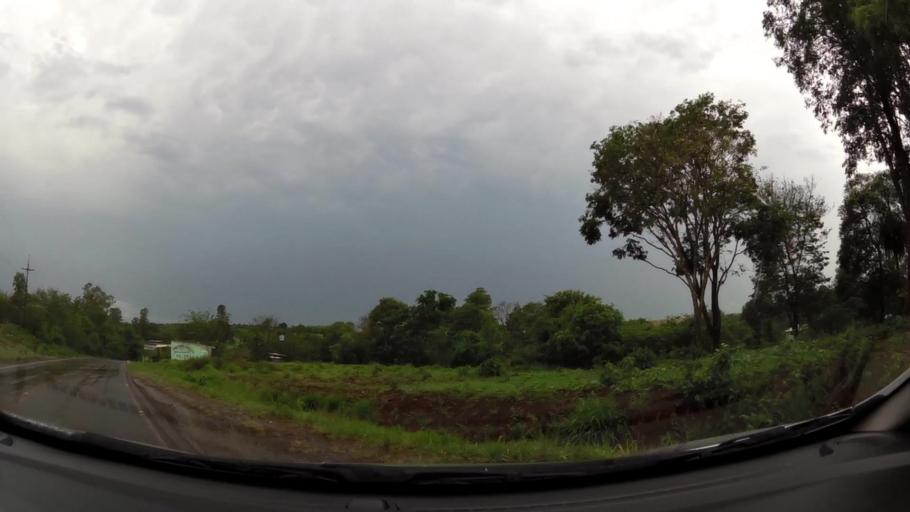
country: PY
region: Alto Parana
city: Los Cedrales
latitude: -25.5840
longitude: -54.6781
